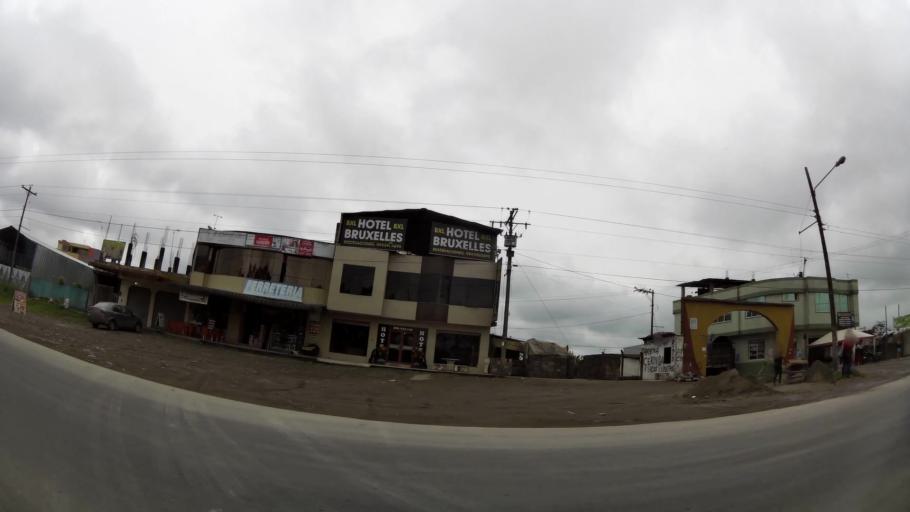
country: EC
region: Santo Domingo de los Tsachilas
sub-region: Canton Santo Domingo de los Colorados
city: Santo Domingo de los Colorados
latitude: -0.2321
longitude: -79.1641
